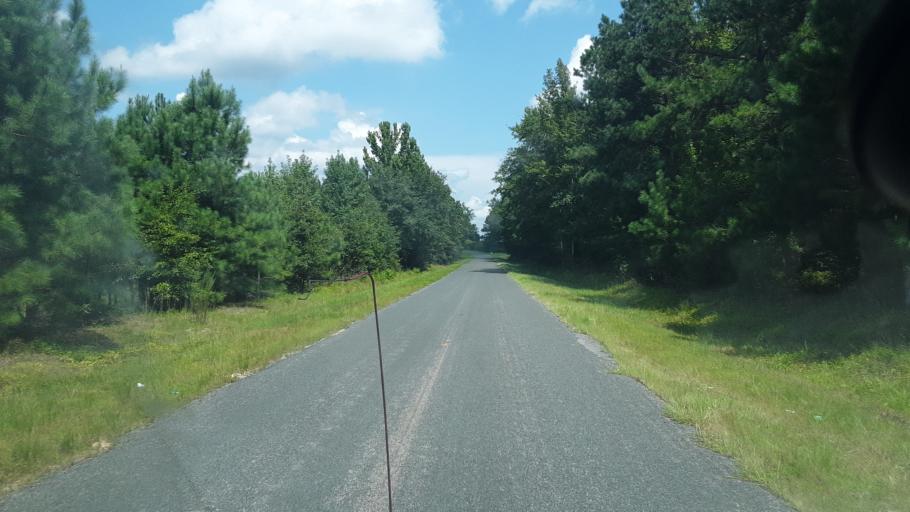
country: US
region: South Carolina
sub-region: Calhoun County
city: Oak Grove
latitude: 33.6685
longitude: -80.9725
